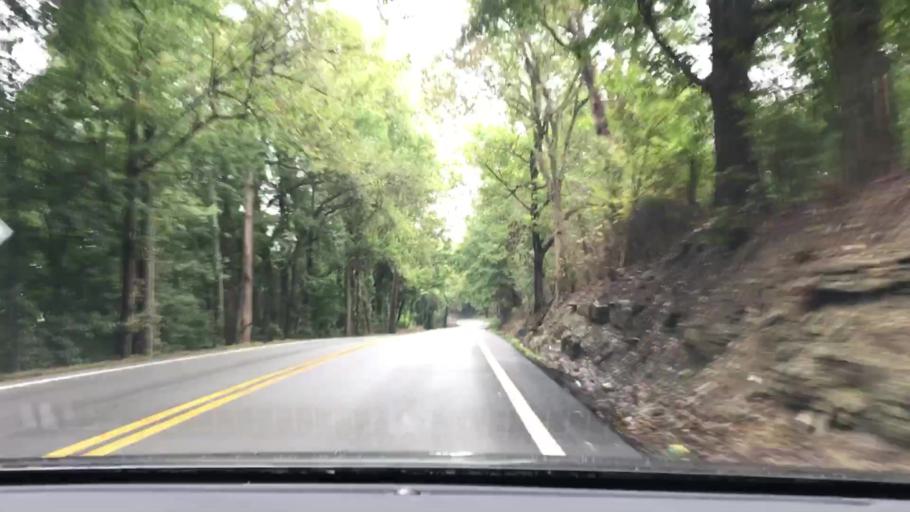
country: US
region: Tennessee
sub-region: Macon County
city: Red Boiling Springs
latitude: 36.5624
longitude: -85.7979
